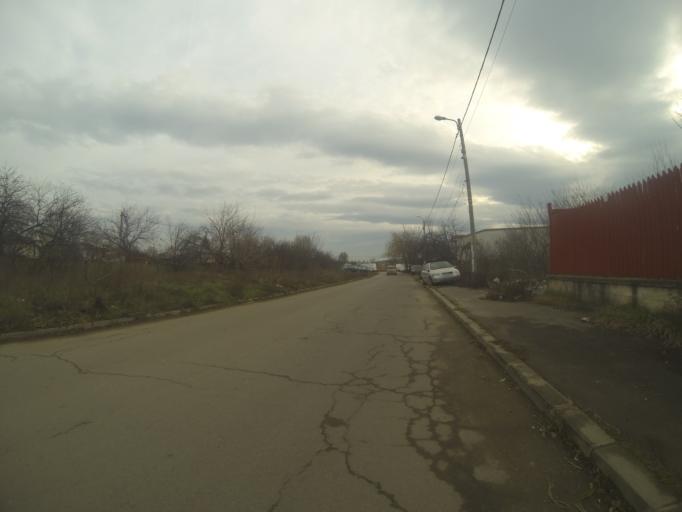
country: RO
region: Ilfov
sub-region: Comuna Jilava
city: Jilava
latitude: 44.3731
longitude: 26.0868
